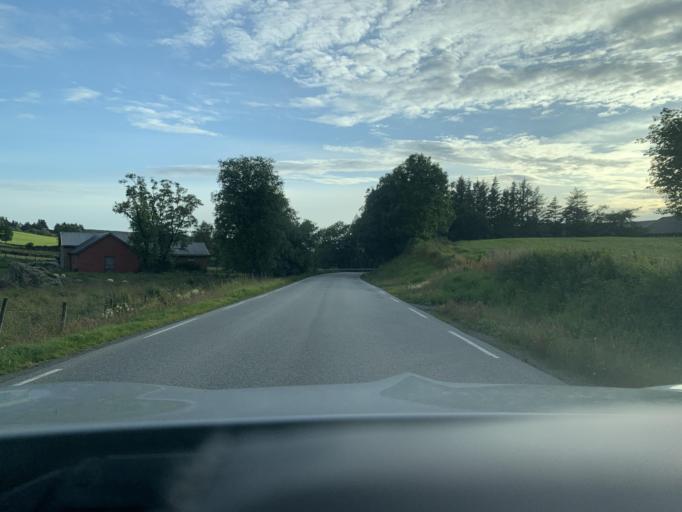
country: NO
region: Rogaland
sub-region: Ha
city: Varhaug
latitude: 58.6847
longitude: 5.7546
